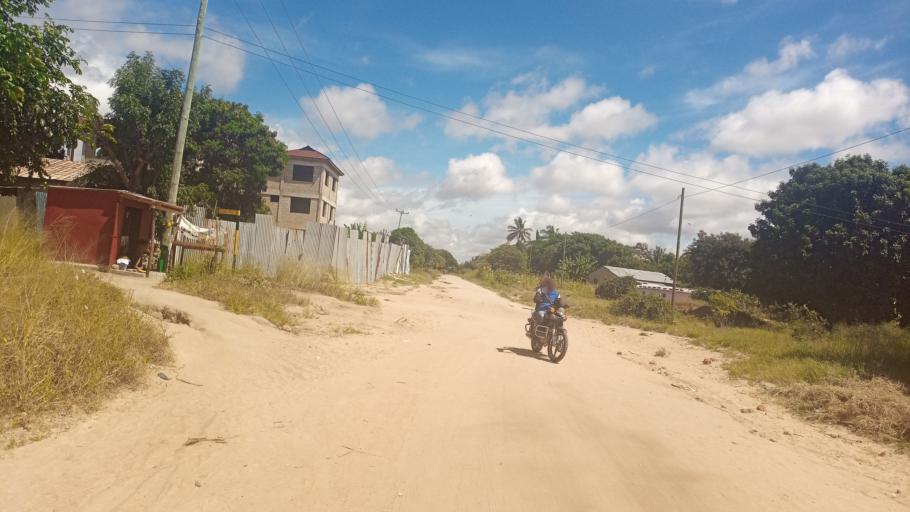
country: TZ
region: Dodoma
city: Dodoma
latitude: -6.1953
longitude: 35.7263
